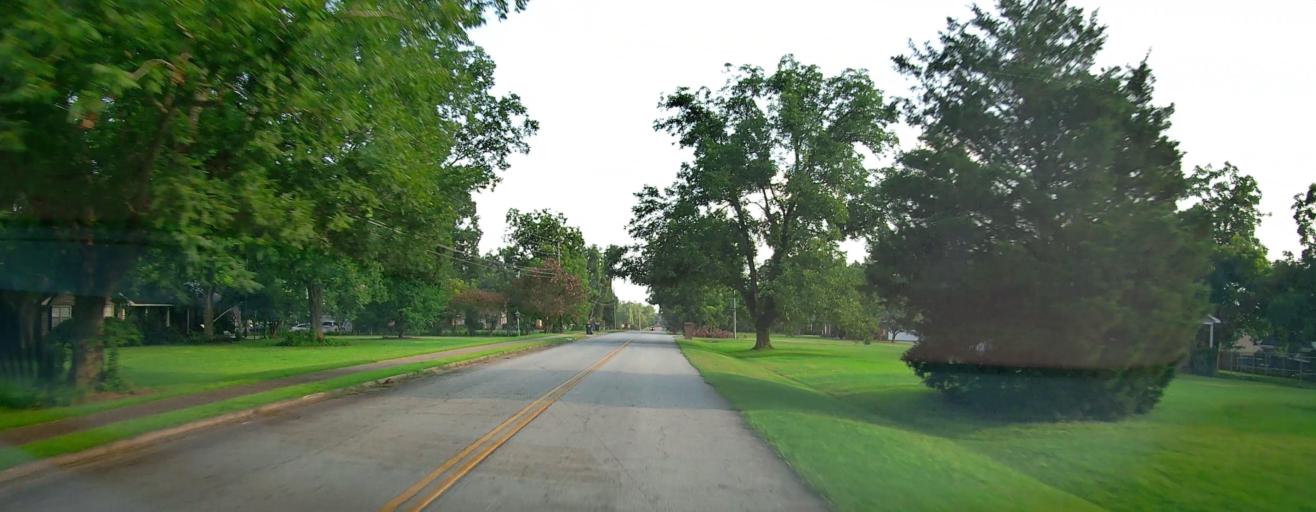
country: US
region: Georgia
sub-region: Peach County
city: Byron
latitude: 32.7417
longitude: -83.6937
